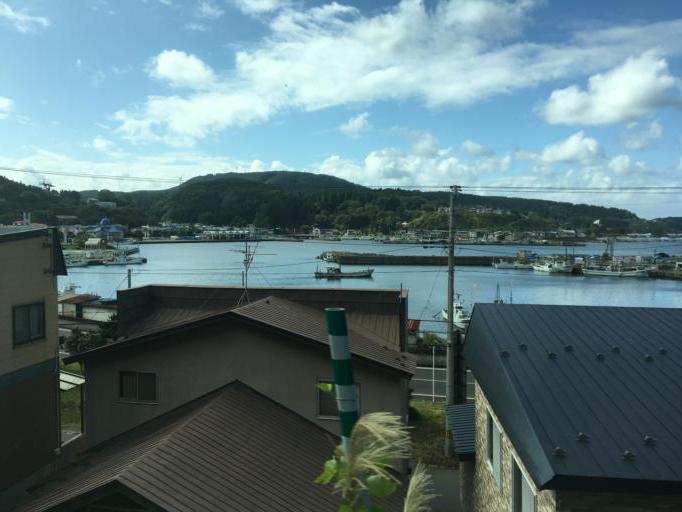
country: JP
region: Akita
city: Noshiromachi
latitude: 40.6456
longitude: 139.9306
